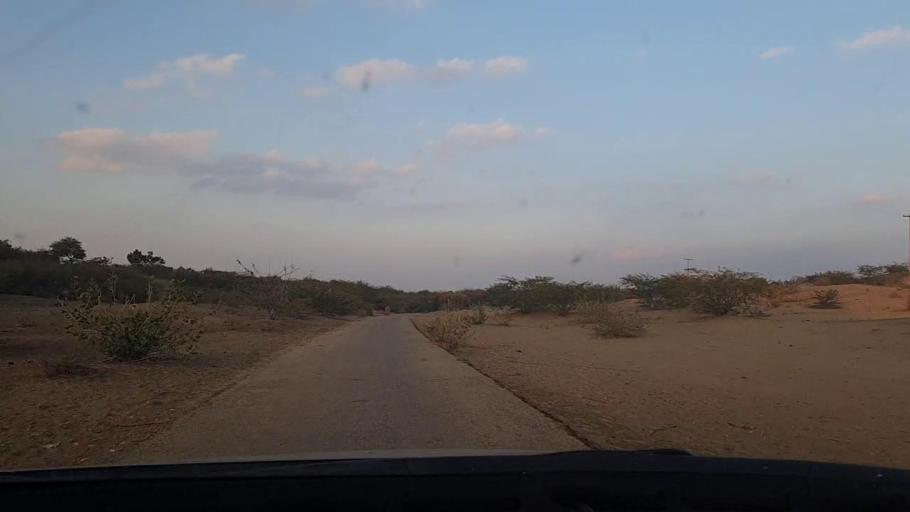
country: PK
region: Sindh
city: Tando Mittha Khan
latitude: 25.9421
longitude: 69.3408
